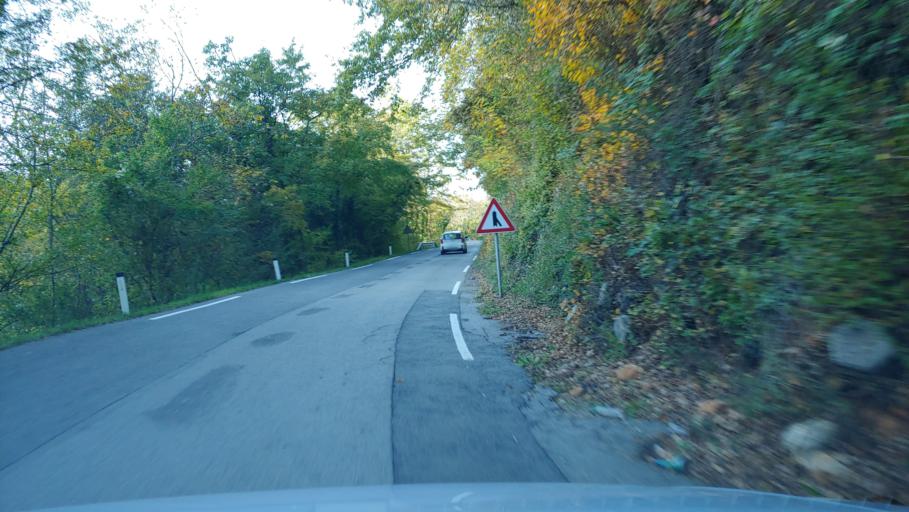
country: SI
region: Ajdovscina
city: Ajdovscina
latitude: 45.8039
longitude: 13.8666
